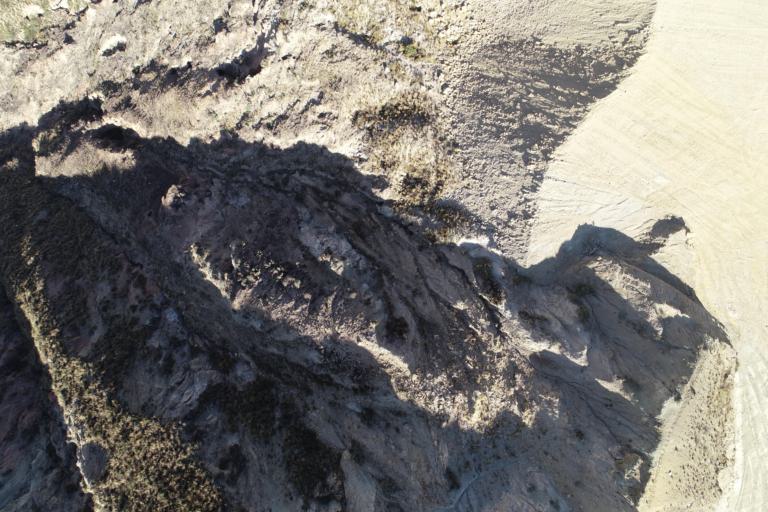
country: BO
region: La Paz
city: La Paz
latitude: -16.5496
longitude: -68.1058
